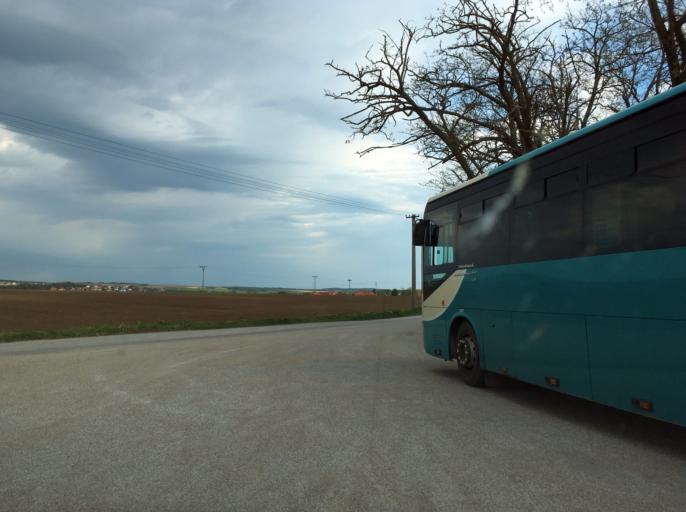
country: SK
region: Nitriansky
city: Svodin
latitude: 47.8998
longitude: 18.4005
